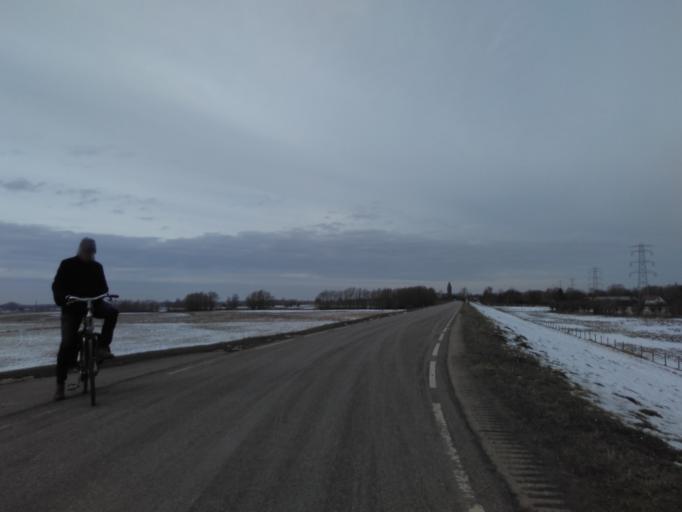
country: NL
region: Gelderland
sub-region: Gemeente Overbetuwe
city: Oosterhout
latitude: 51.8708
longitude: 5.8370
